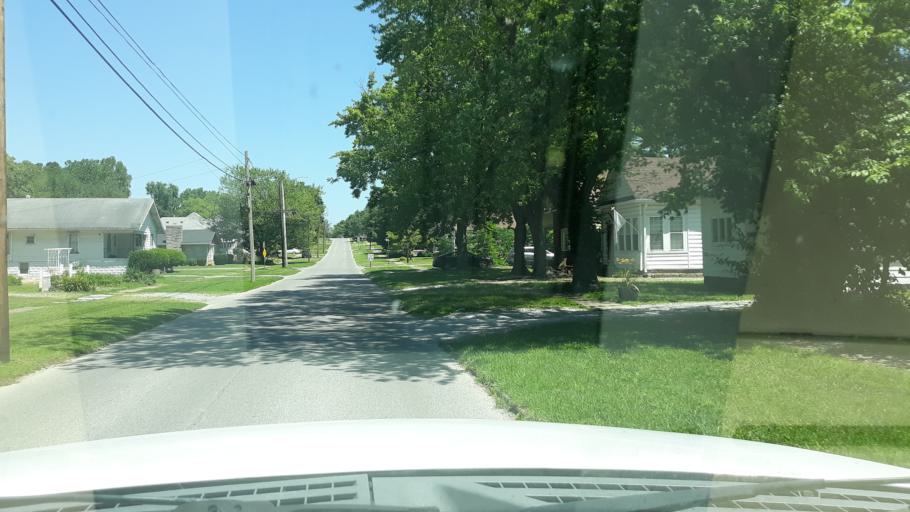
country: US
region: Illinois
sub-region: Saline County
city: Eldorado
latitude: 37.8170
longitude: -88.4361
